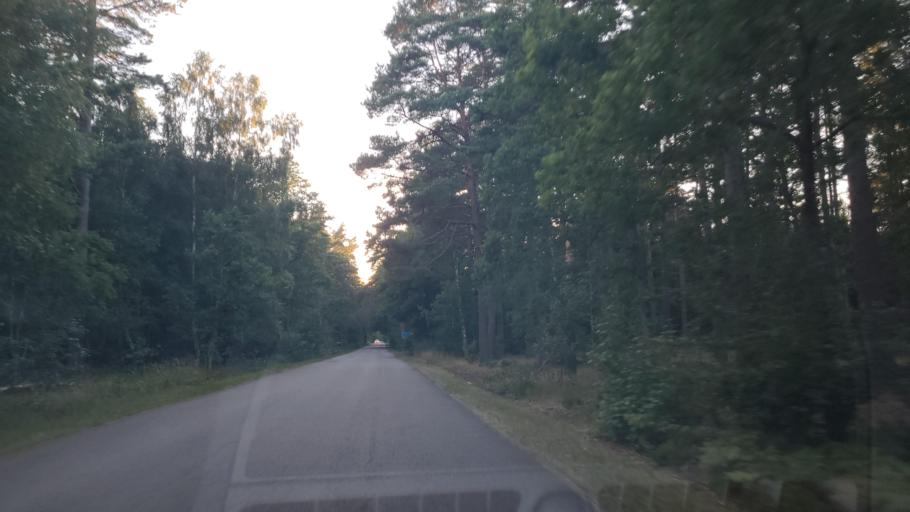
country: SE
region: Kalmar
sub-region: Borgholms Kommun
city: Borgholm
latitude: 57.2770
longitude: 17.0345
